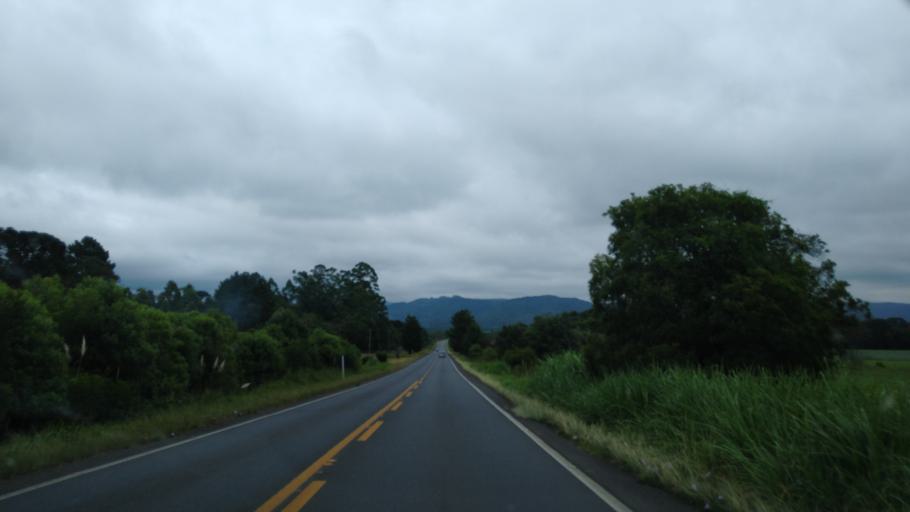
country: BR
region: Santa Catarina
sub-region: Porto Uniao
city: Porto Uniao
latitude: -26.2833
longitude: -51.0077
